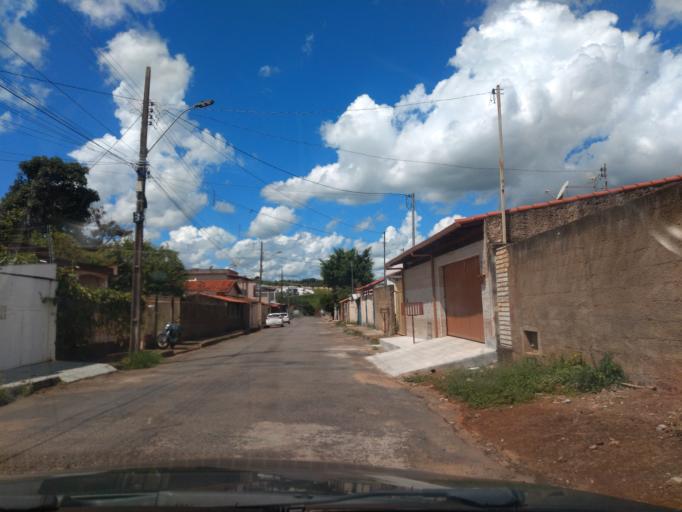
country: BR
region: Minas Gerais
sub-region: Tres Coracoes
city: Tres Coracoes
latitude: -21.6817
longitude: -45.2602
